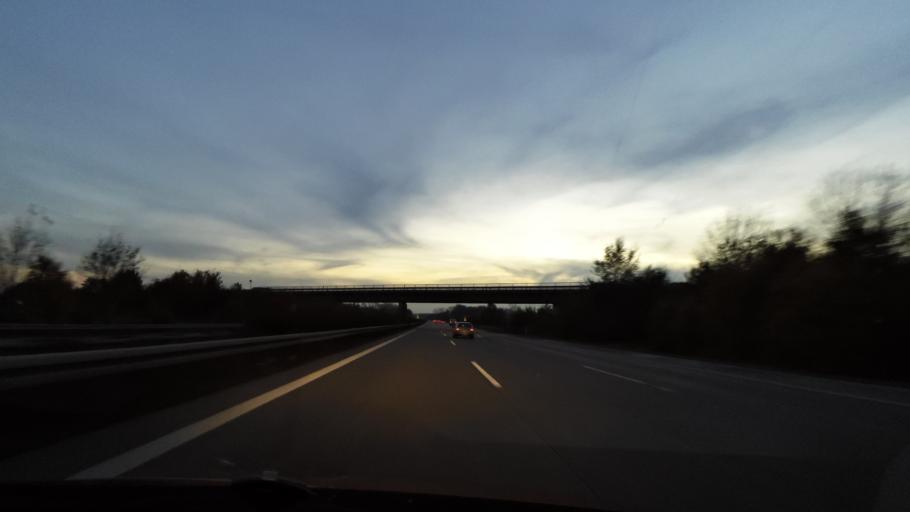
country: DE
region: Saxony-Anhalt
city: Tollwitz
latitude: 51.2831
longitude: 12.1256
